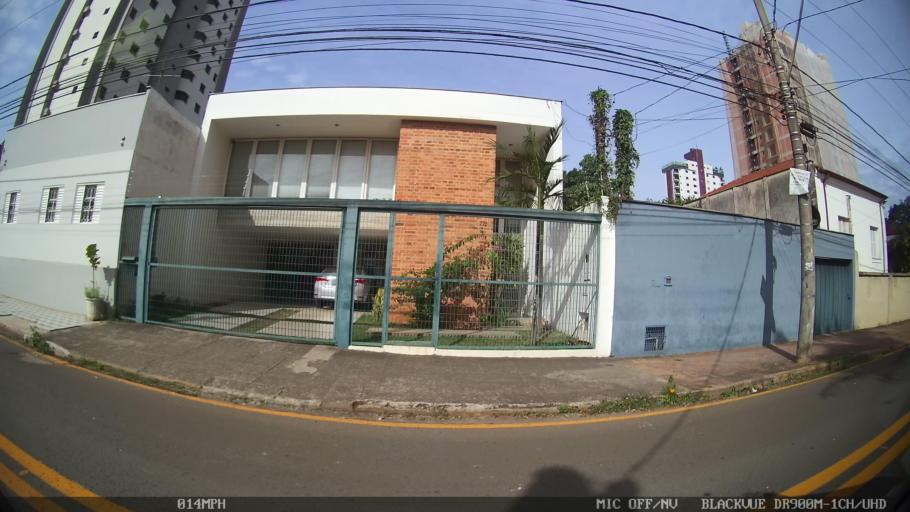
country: BR
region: Sao Paulo
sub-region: Piracicaba
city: Piracicaba
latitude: -22.7138
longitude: -47.6360
